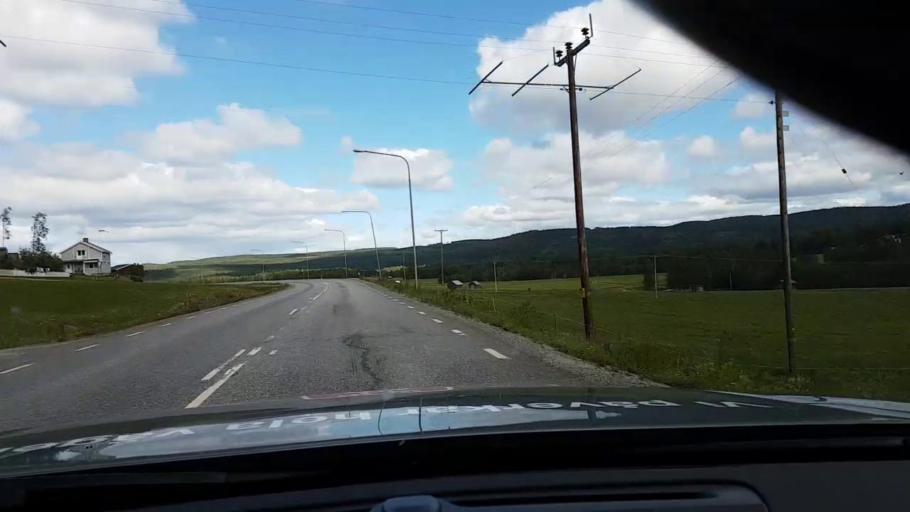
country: SE
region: Vaesternorrland
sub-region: OErnskoeldsviks Kommun
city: Bredbyn
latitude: 63.4958
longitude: 18.0821
